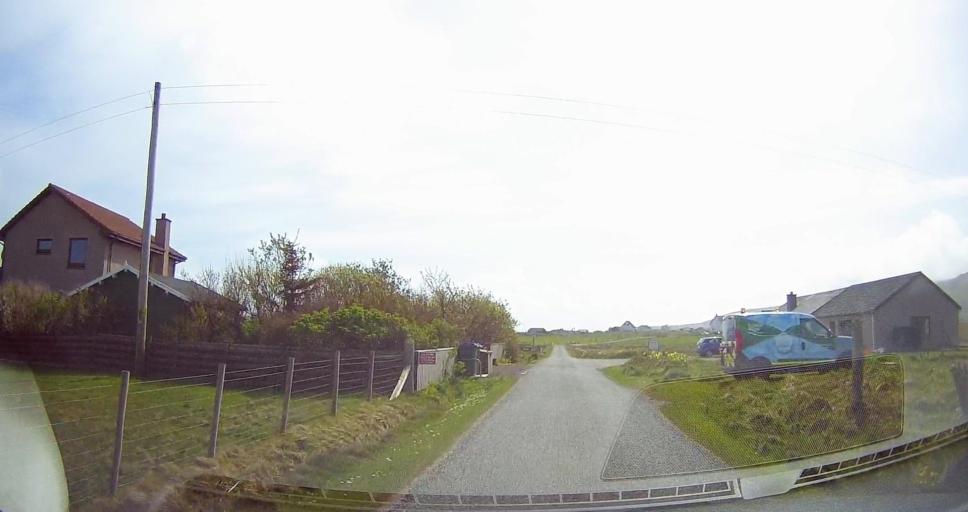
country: GB
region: Scotland
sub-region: Shetland Islands
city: Sandwick
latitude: 60.0445
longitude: -1.2167
